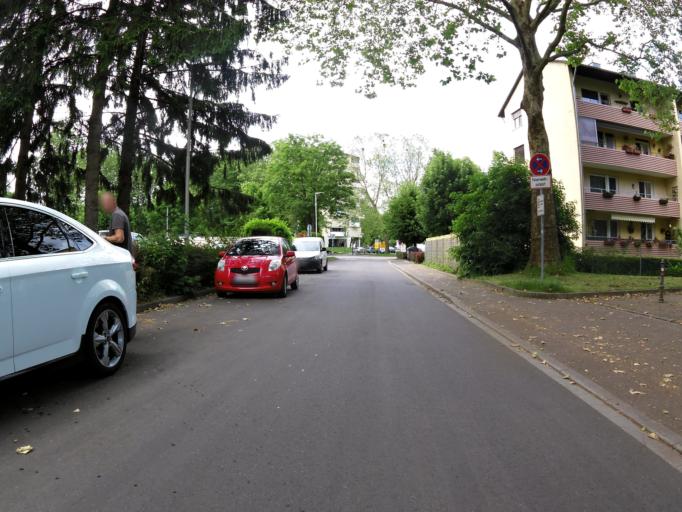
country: DE
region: Baden-Wuerttemberg
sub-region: Freiburg Region
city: Lahr
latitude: 48.3382
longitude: 7.8441
